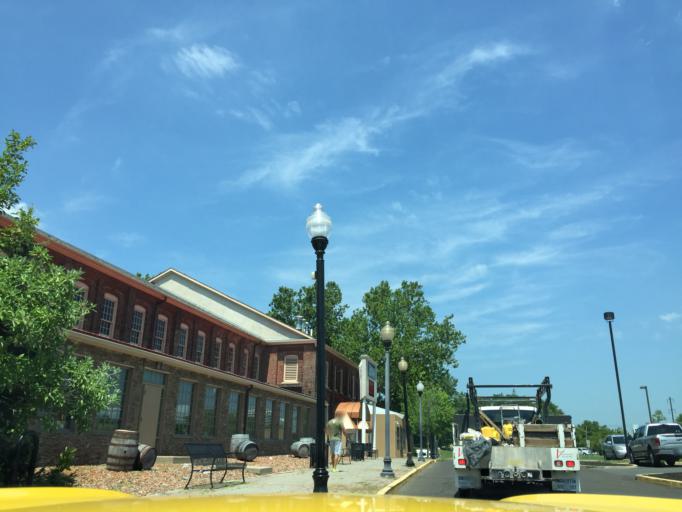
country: US
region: New Jersey
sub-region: Mercer County
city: Trenton
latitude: 40.2066
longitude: -74.7644
